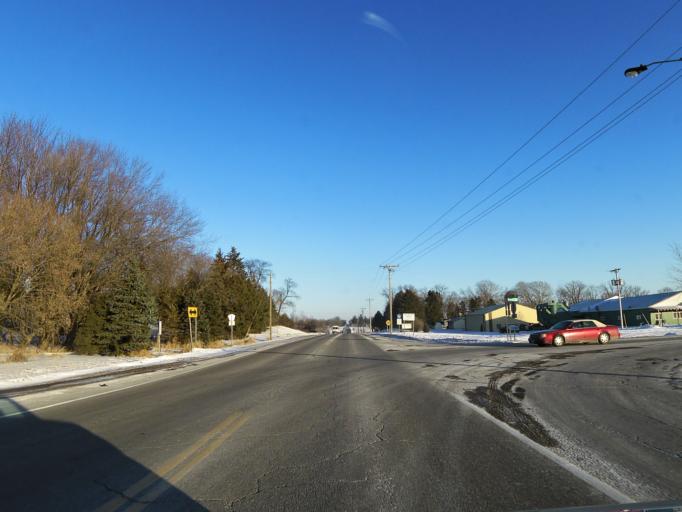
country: US
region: Minnesota
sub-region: Rice County
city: Northfield
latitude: 44.5438
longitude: -93.2015
